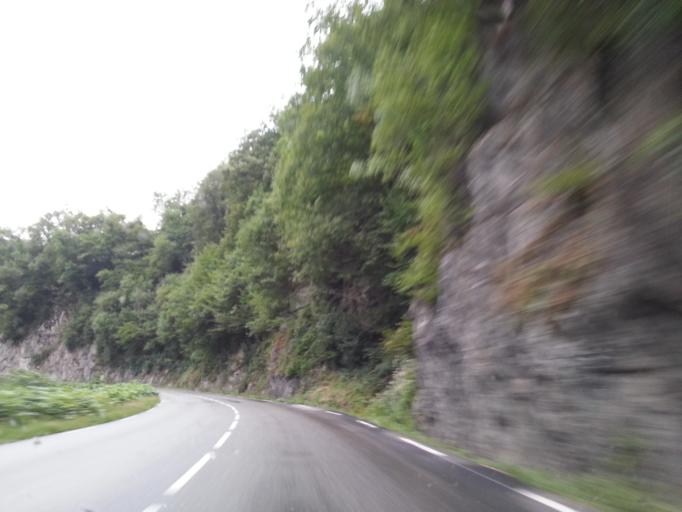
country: FR
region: Rhone-Alpes
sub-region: Departement de la Savoie
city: Marthod
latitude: 45.7169
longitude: 6.4666
